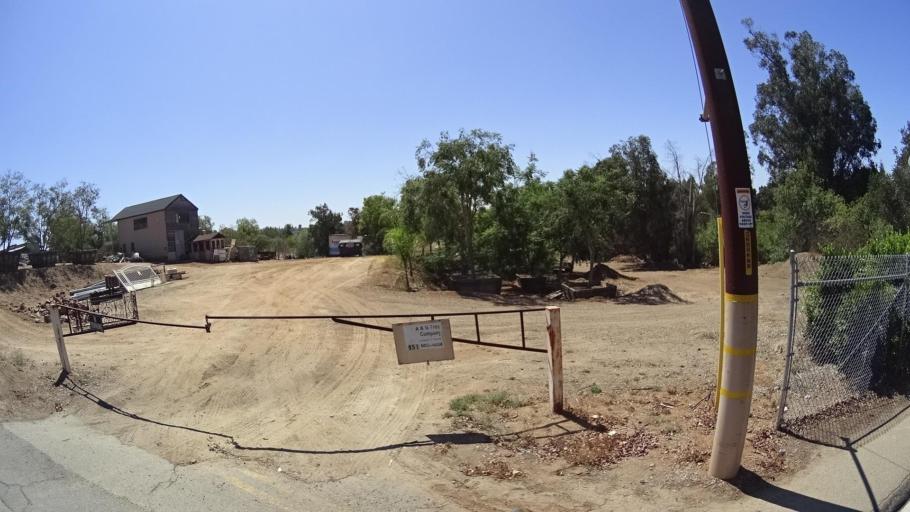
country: US
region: California
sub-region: San Diego County
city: Fallbrook
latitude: 33.3692
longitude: -117.2251
